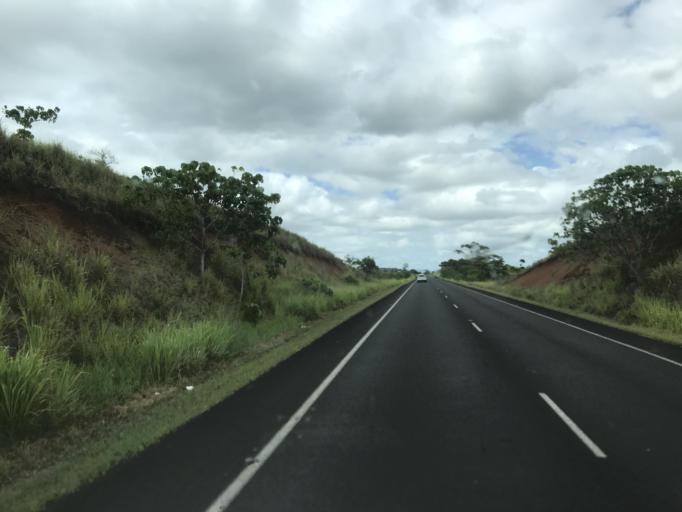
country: AU
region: Queensland
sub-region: Cassowary Coast
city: Innisfail
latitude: -17.5787
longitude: 145.9823
